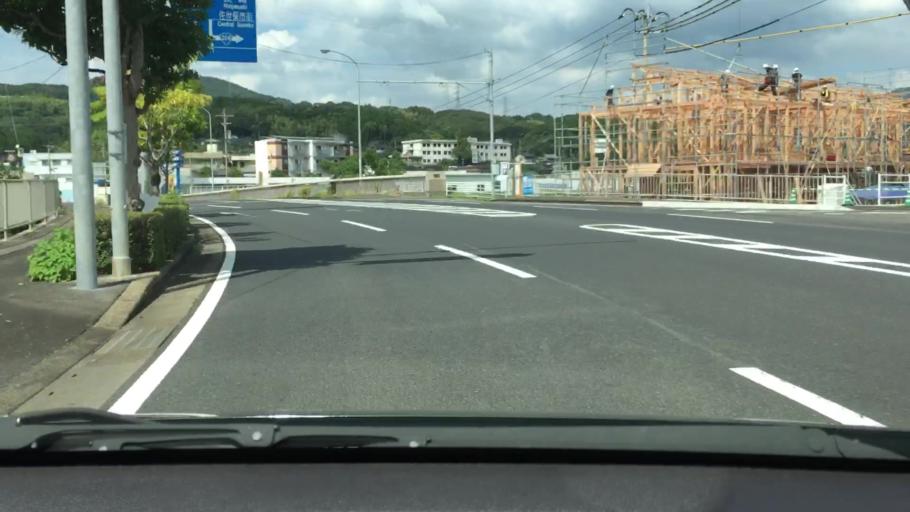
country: JP
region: Nagasaki
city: Sasebo
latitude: 33.2042
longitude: 129.6807
